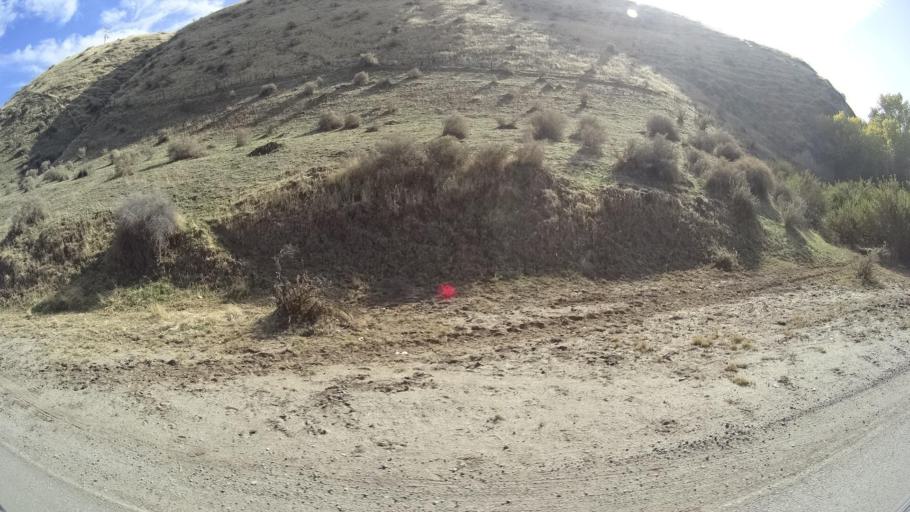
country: US
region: California
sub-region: Kern County
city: Oildale
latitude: 35.5142
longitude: -118.9056
